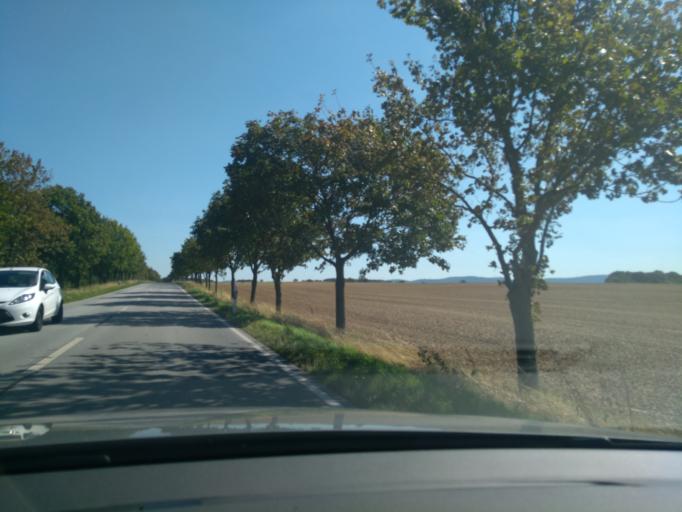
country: DE
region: Saxony
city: Goda
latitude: 51.1999
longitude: 14.3169
